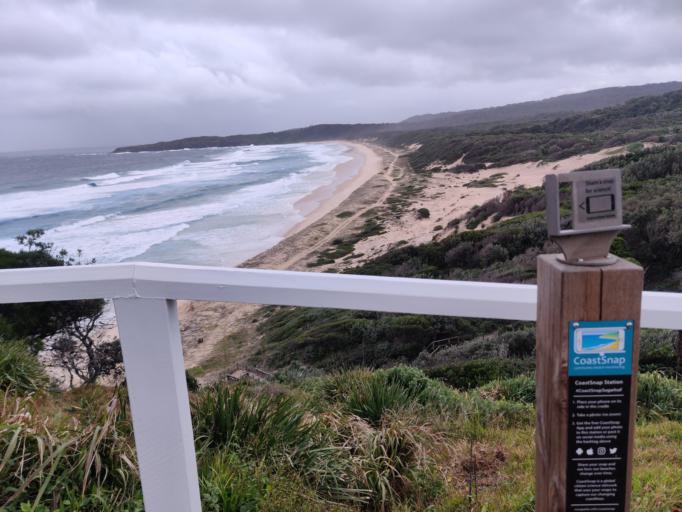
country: AU
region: New South Wales
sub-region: Great Lakes
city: Forster
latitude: -32.4412
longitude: 152.5380
